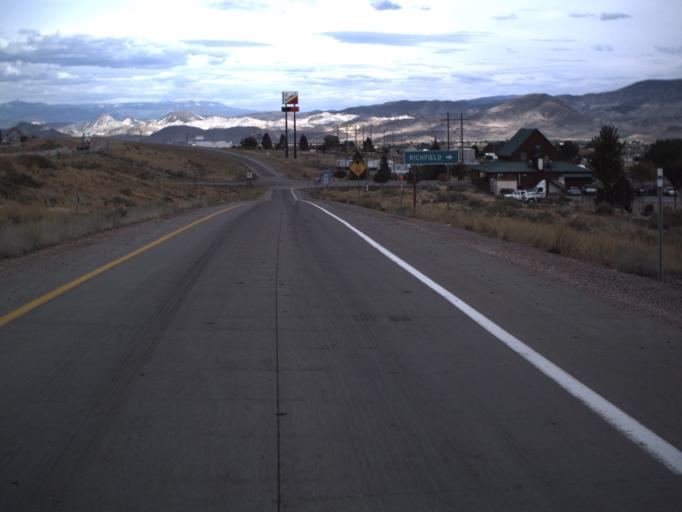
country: US
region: Utah
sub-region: Sevier County
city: Richfield
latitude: 38.7881
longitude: -112.0865
